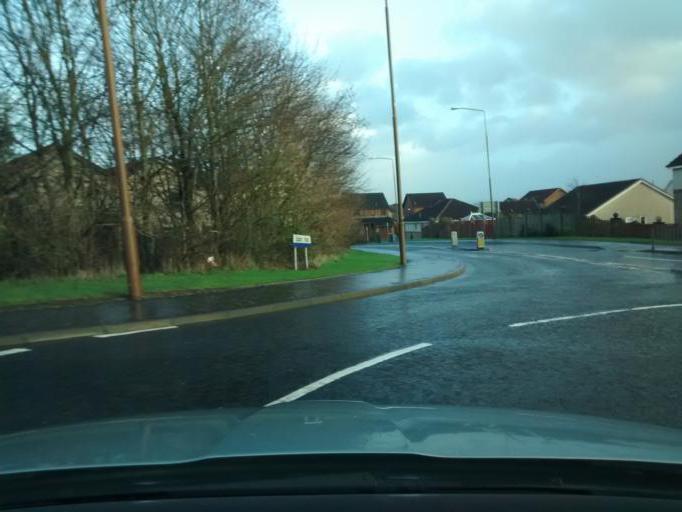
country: GB
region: Scotland
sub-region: West Lothian
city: Livingston
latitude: 55.8896
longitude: -3.5505
